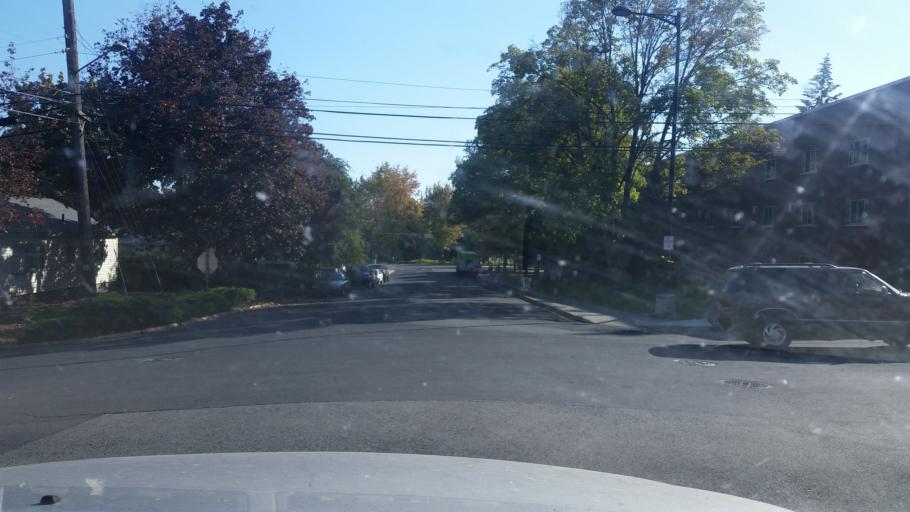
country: US
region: Washington
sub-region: Spokane County
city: Cheney
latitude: 47.4939
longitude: -117.5823
